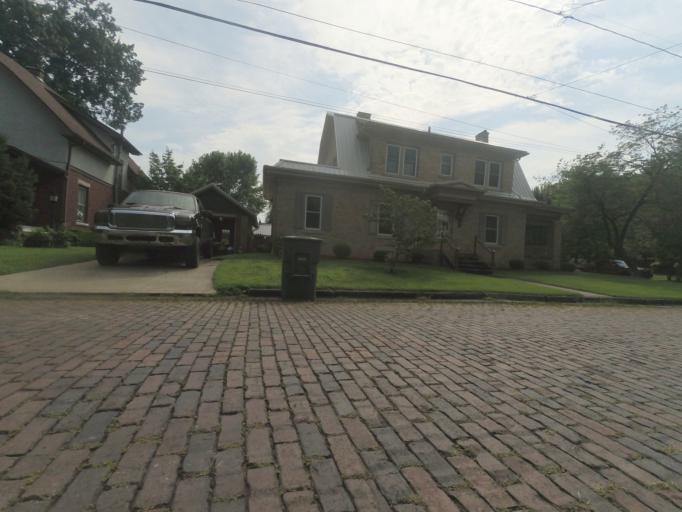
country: US
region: West Virginia
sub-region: Cabell County
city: Huntington
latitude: 38.4070
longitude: -82.4585
